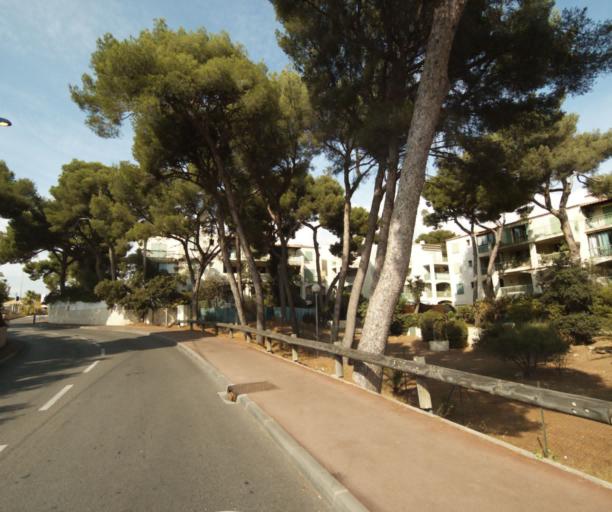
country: FR
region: Provence-Alpes-Cote d'Azur
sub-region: Departement des Bouches-du-Rhone
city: Sausset-les-Pins
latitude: 43.3318
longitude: 5.1253
